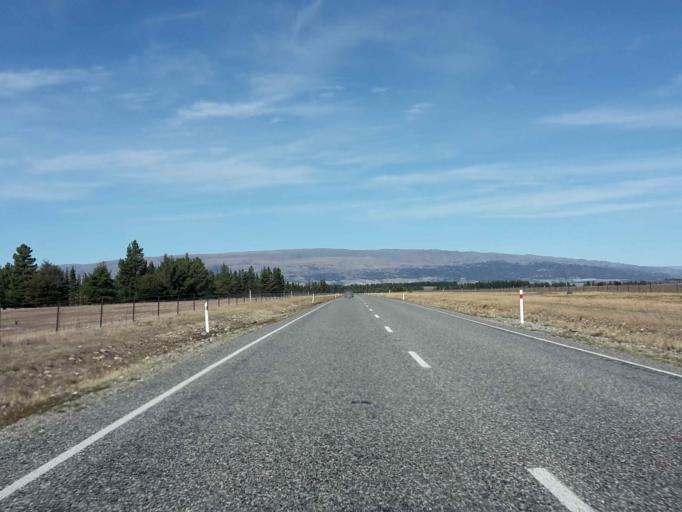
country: NZ
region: Otago
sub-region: Queenstown-Lakes District
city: Wanaka
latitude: -44.7902
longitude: 169.3561
